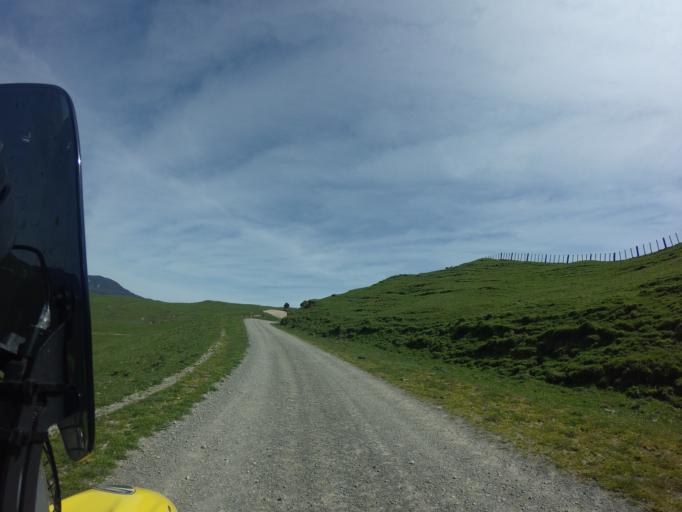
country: NZ
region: Bay of Plenty
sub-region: Opotiki District
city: Opotiki
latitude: -38.4538
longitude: 177.3610
